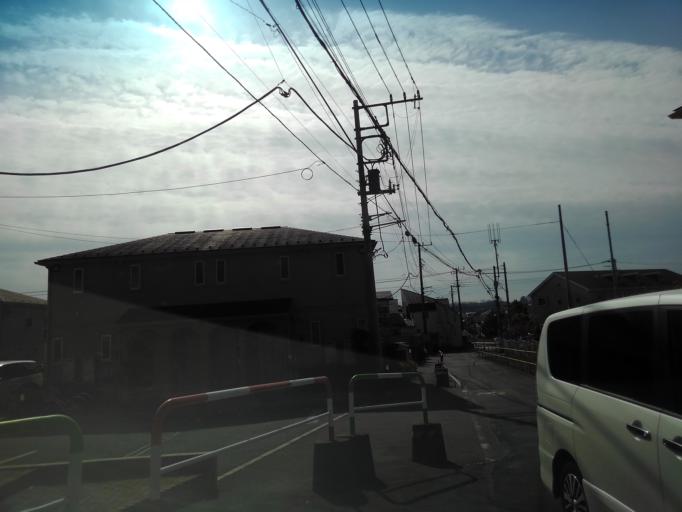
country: JP
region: Saitama
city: Tokorozawa
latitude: 35.7898
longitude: 139.5126
